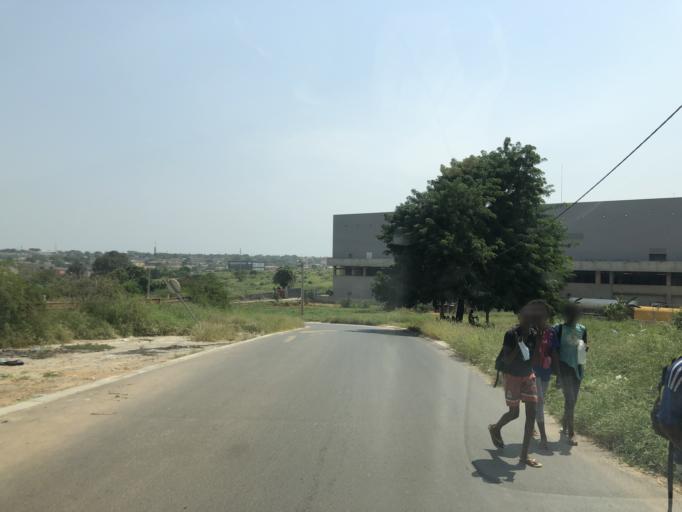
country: AO
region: Luanda
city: Luanda
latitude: -8.8991
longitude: 13.2259
